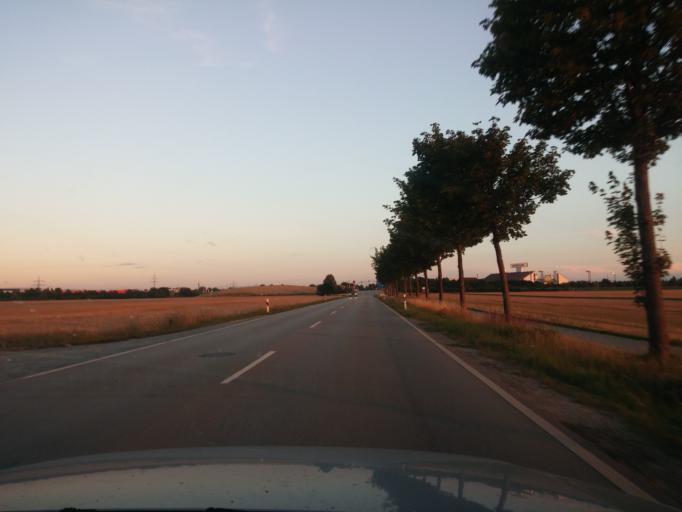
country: DE
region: Bavaria
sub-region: Upper Bavaria
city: Poing
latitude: 48.1536
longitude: 11.7857
